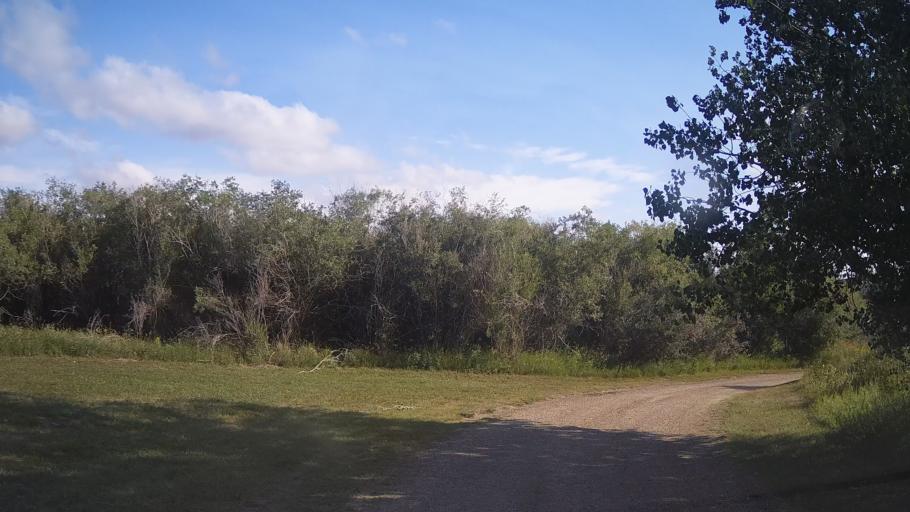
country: CA
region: Alberta
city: Brooks
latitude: 50.9173
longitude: -111.8996
